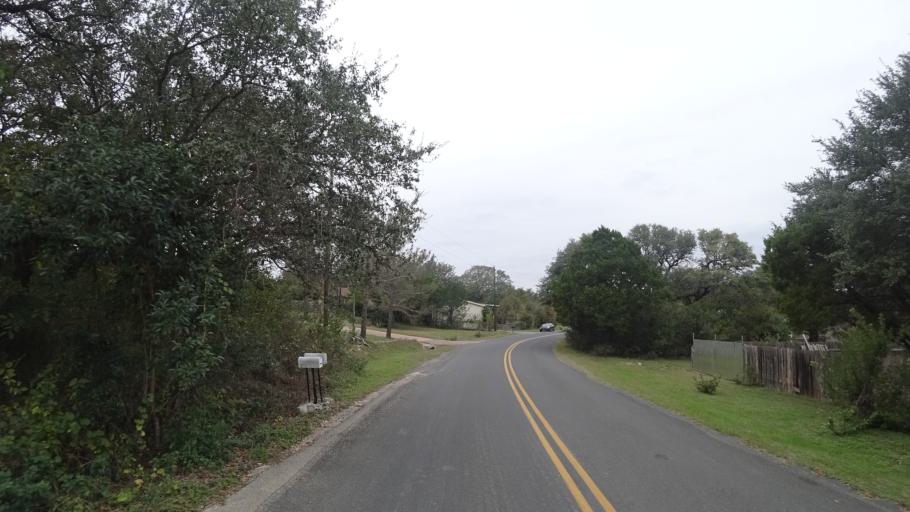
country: US
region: Texas
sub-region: Travis County
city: Lakeway
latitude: 30.3704
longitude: -97.9378
